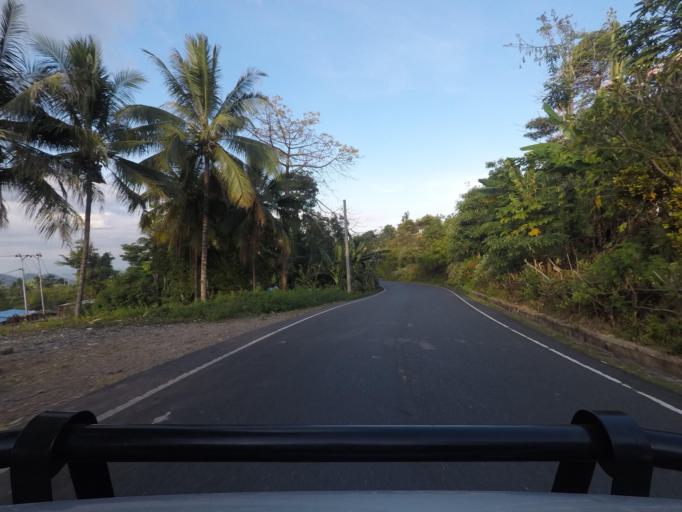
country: TL
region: Bobonaro
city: Maliana
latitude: -8.9576
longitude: 125.0620
